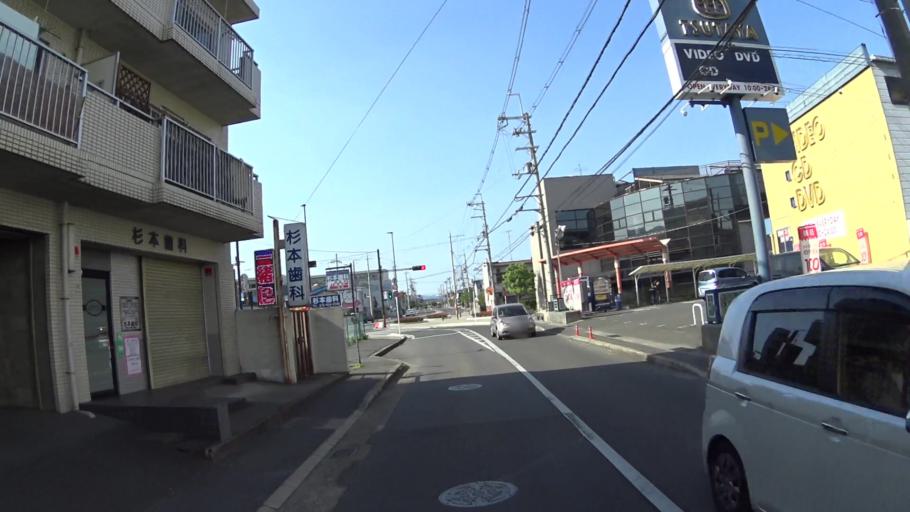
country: JP
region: Kyoto
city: Yawata
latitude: 34.9171
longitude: 135.6889
